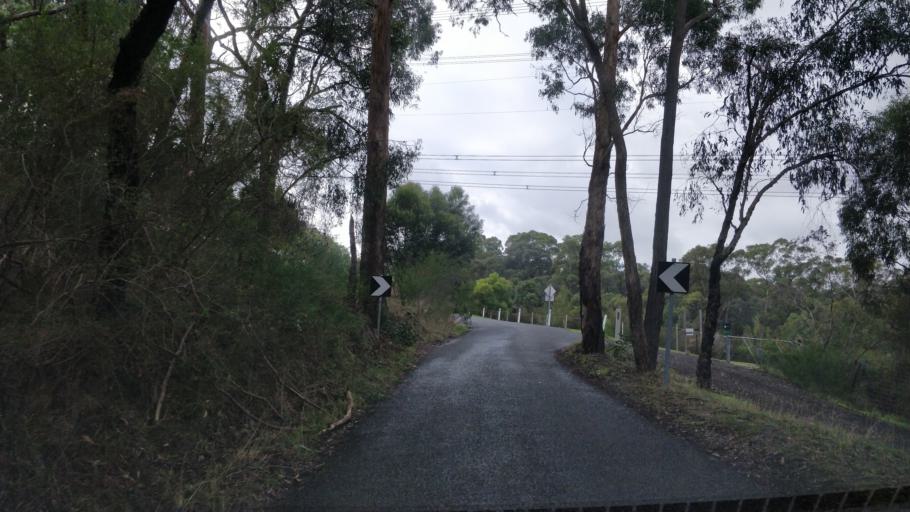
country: AU
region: Victoria
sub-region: Nillumbik
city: Research
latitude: -37.7168
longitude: 145.1705
